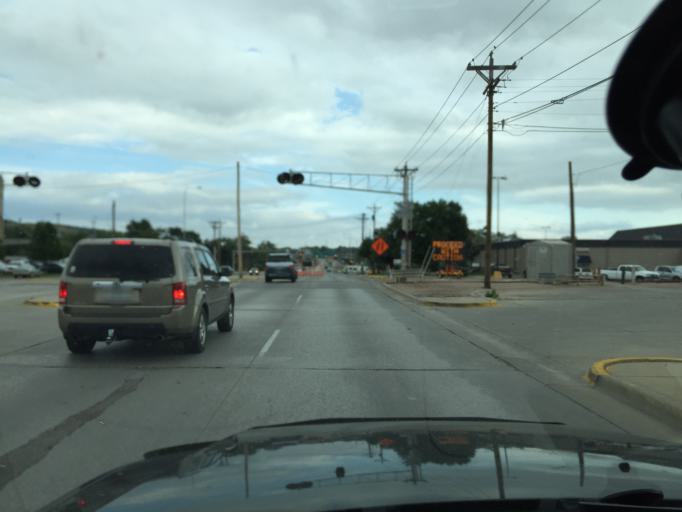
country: US
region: South Dakota
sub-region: Pennington County
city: Rapid City
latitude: 44.0825
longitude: -103.2345
